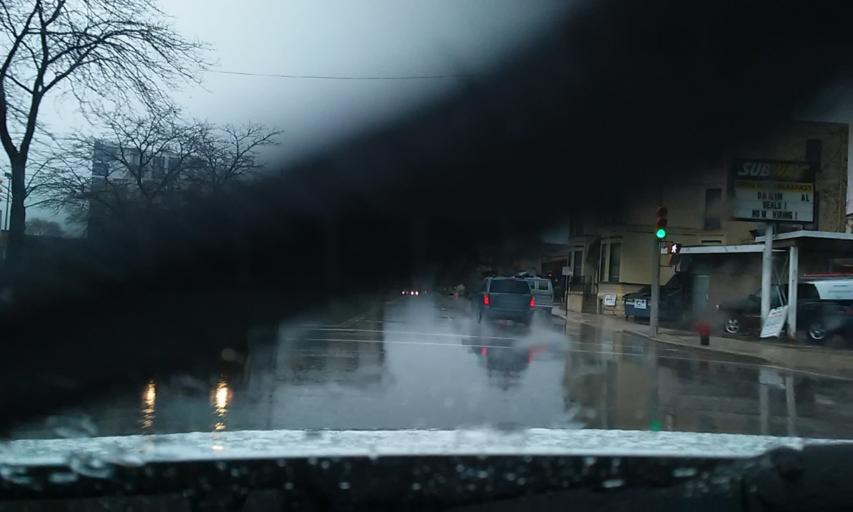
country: US
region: Wisconsin
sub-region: Milwaukee County
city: Milwaukee
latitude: 43.0457
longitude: -87.9035
